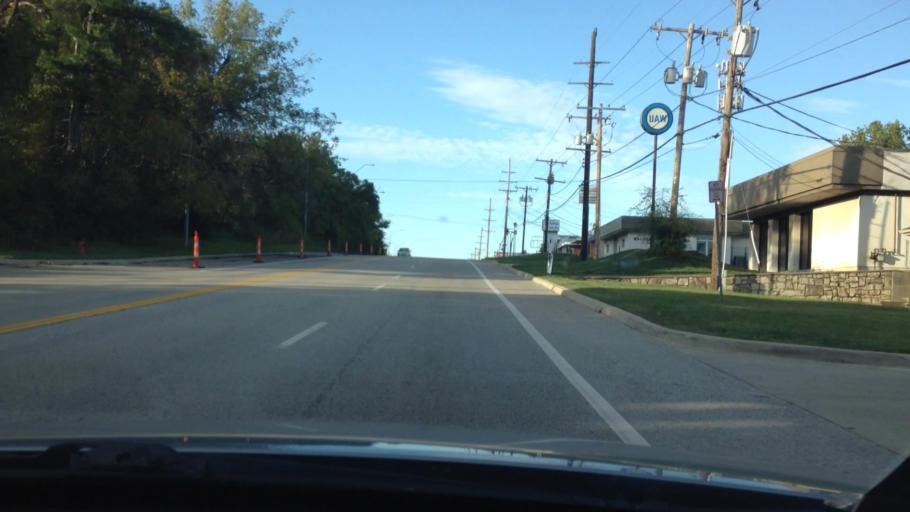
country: US
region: Missouri
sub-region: Clay County
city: North Kansas City
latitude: 39.1639
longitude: -94.5768
